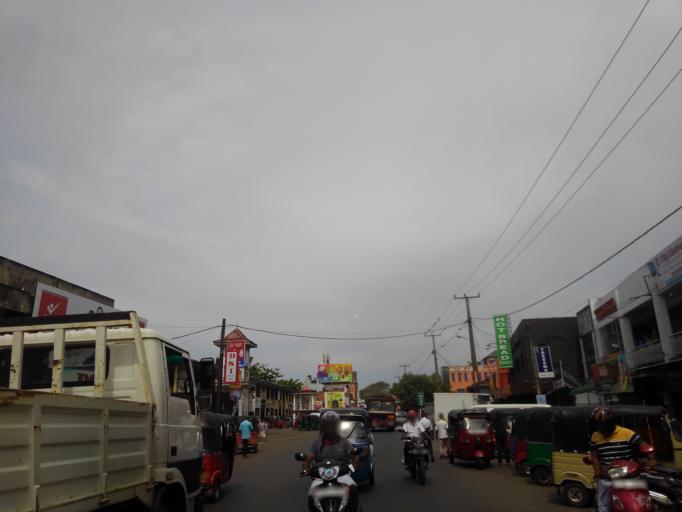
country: LK
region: Western
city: Beruwala
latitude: 6.4749
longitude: 79.9837
